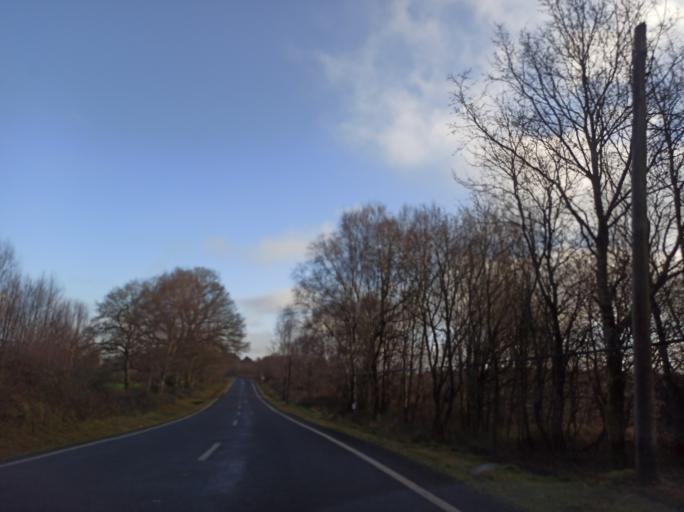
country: ES
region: Galicia
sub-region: Provincia da Coruna
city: Sobrado
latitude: 43.0850
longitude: -8.0009
